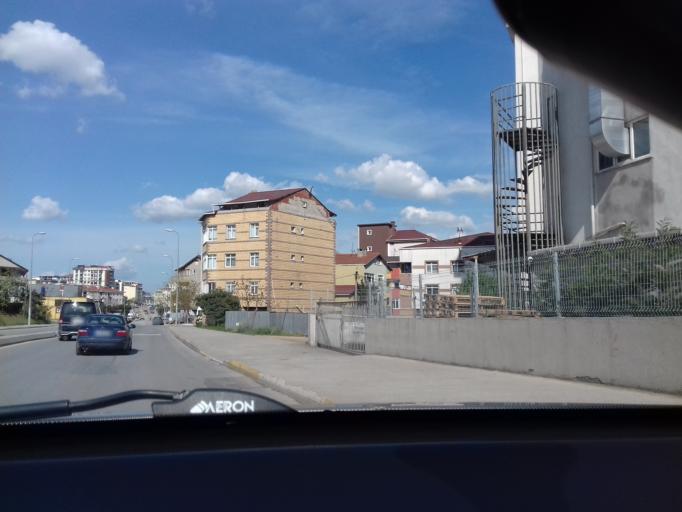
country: TR
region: Istanbul
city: Pendik
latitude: 40.8919
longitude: 29.2696
